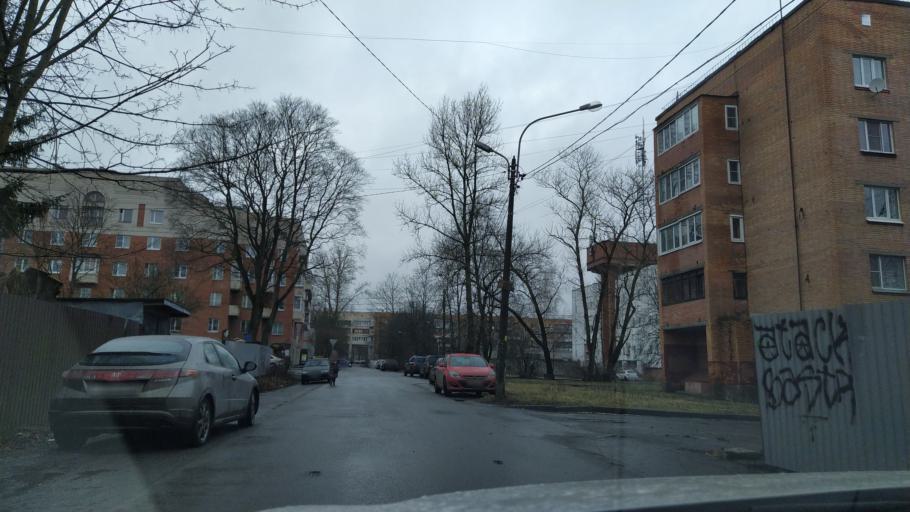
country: RU
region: St.-Petersburg
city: Pushkin
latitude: 59.7270
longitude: 30.4087
